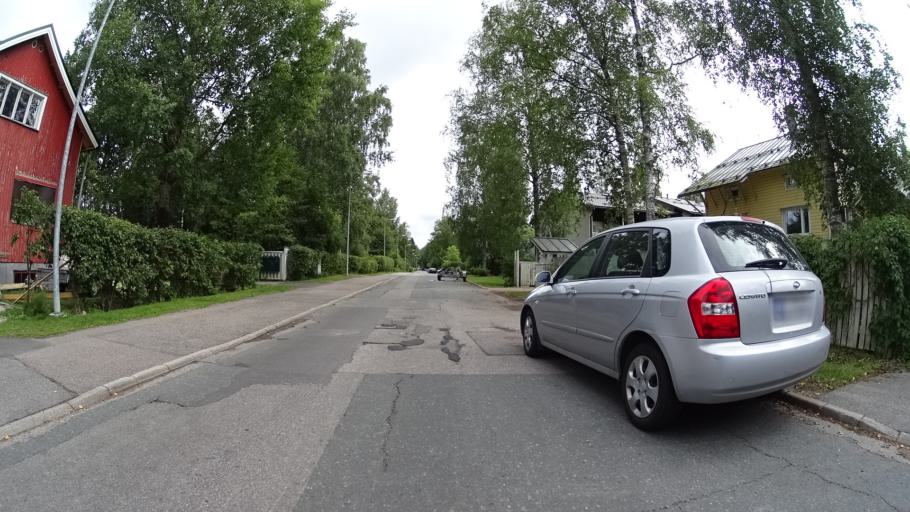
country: FI
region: Uusimaa
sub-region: Helsinki
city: Helsinki
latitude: 60.2534
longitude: 24.9193
